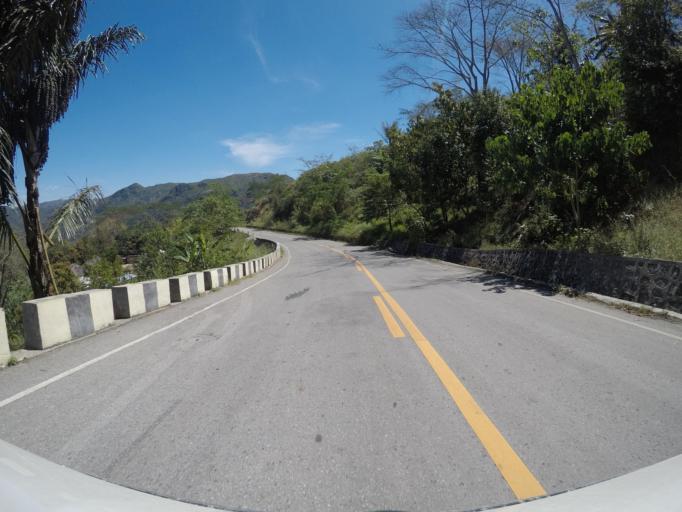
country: TL
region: Manatuto
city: Manatuto
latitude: -8.7833
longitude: 125.9682
